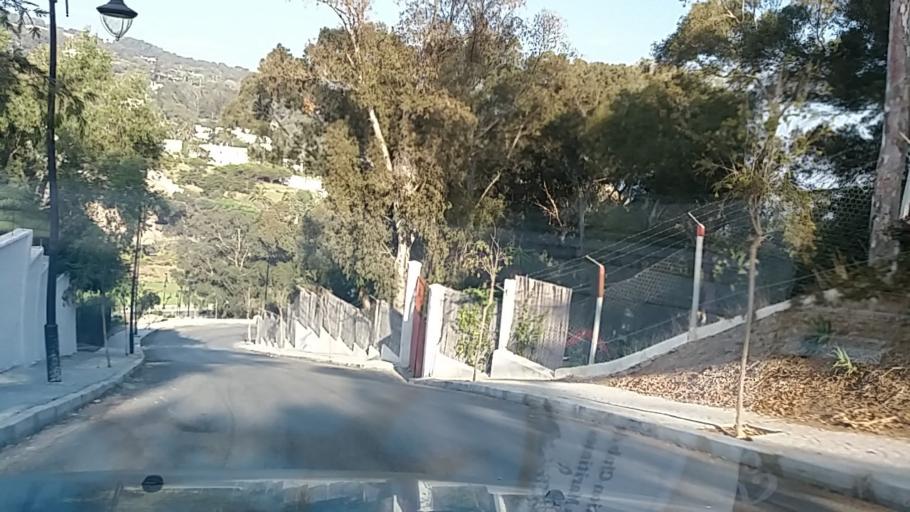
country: MA
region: Tanger-Tetouan
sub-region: Tanger-Assilah
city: Tangier
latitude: 35.7907
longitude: -5.8320
